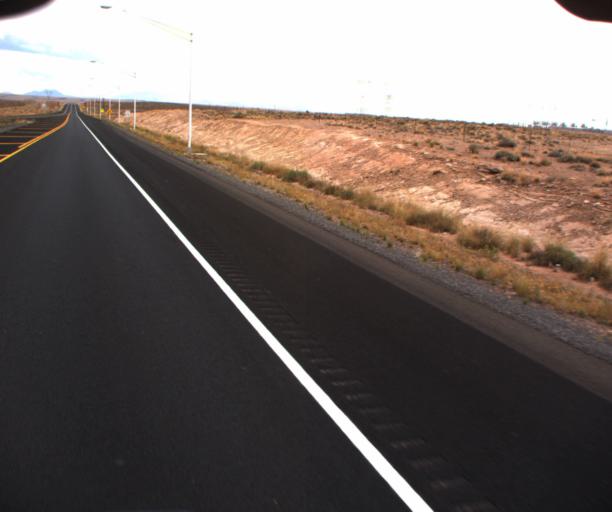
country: US
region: Arizona
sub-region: Coconino County
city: Tuba City
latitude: 35.8374
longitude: -111.4365
